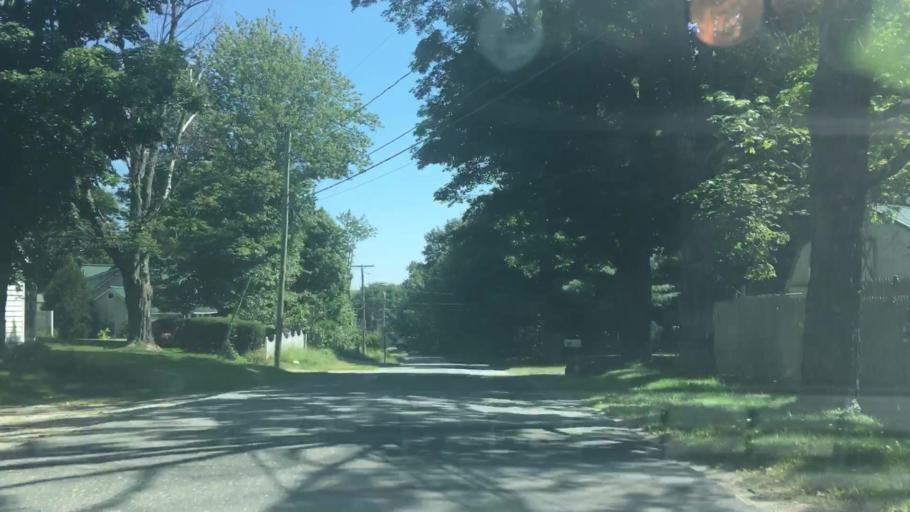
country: US
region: Maine
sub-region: Androscoggin County
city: Sabattus
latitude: 44.1183
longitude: -70.1046
